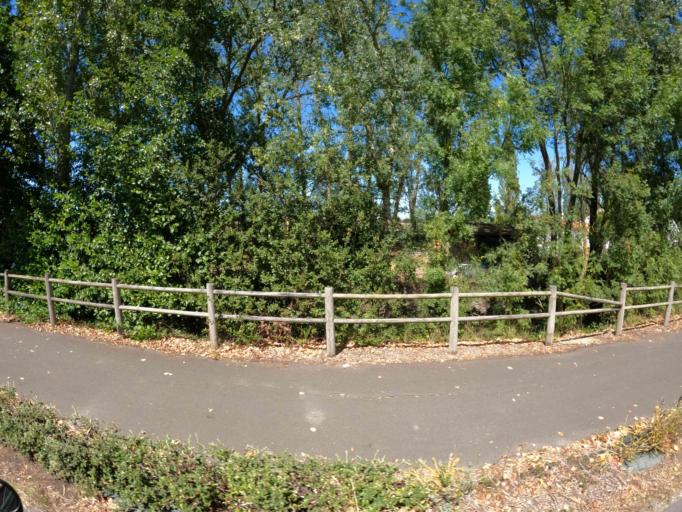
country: FR
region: Pays de la Loire
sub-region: Departement de la Vendee
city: Le Perrier
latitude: 46.8241
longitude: -1.9666
